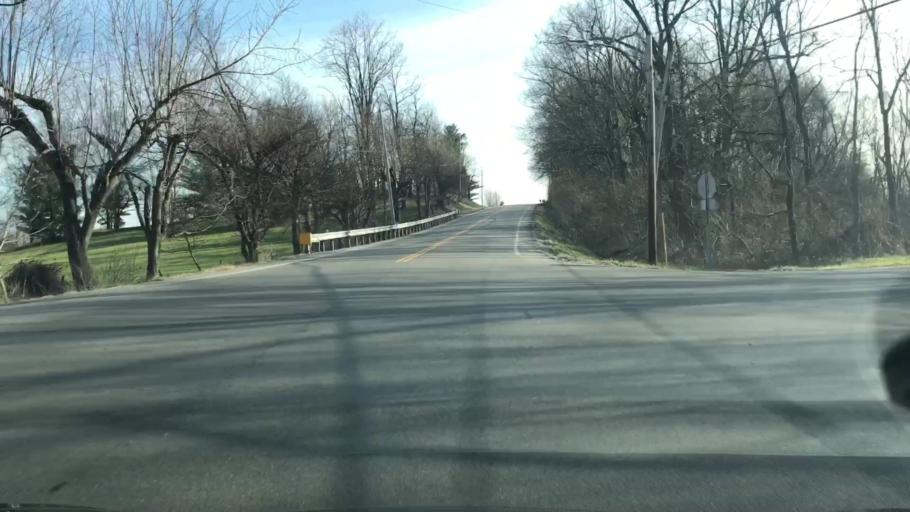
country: US
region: Ohio
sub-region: Greene County
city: Fairborn
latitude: 39.8117
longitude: -83.9810
